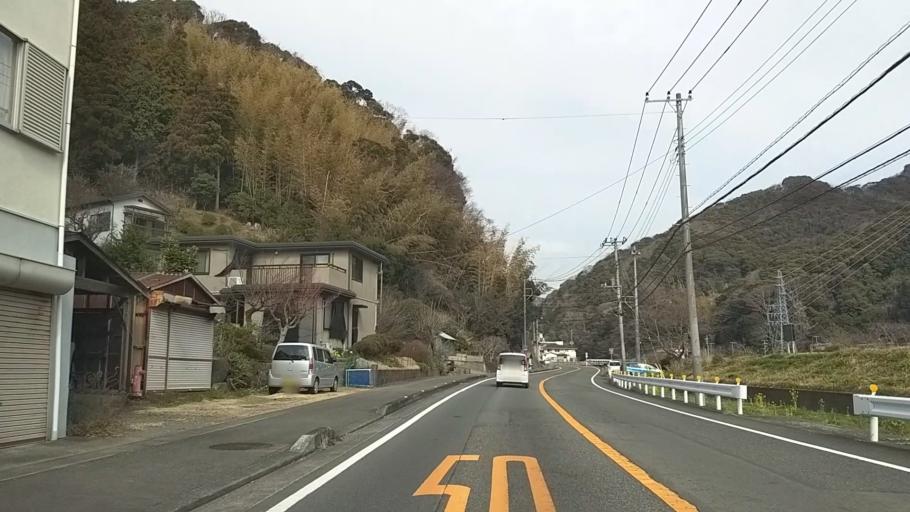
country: JP
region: Shizuoka
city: Shimoda
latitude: 34.7072
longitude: 138.9450
